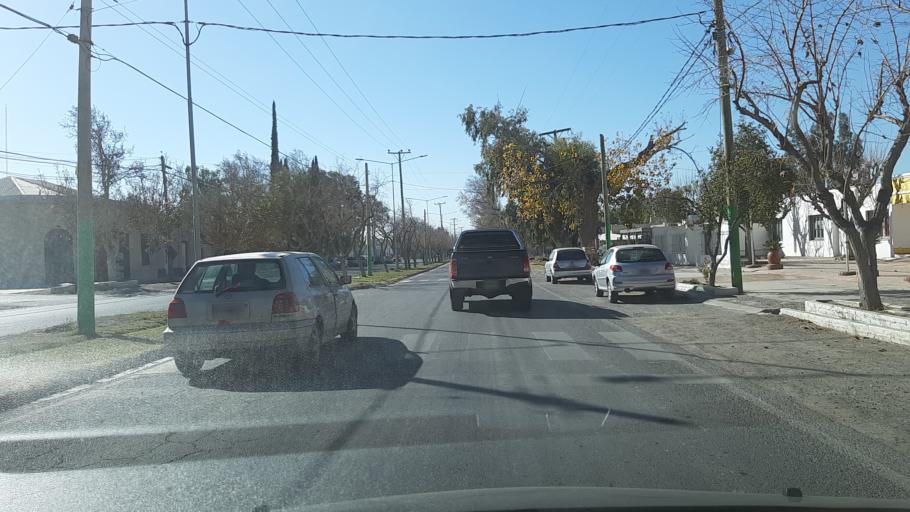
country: AR
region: San Juan
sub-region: Departamento de Rivadavia
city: Rivadavia
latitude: -31.5266
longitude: -68.6326
